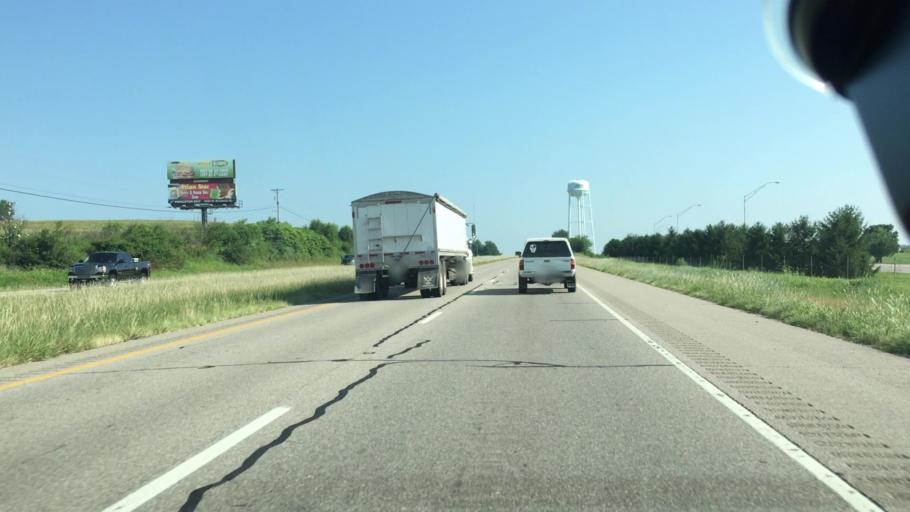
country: US
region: Indiana
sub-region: Gibson County
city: Fort Branch
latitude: 38.2852
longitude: -87.5675
